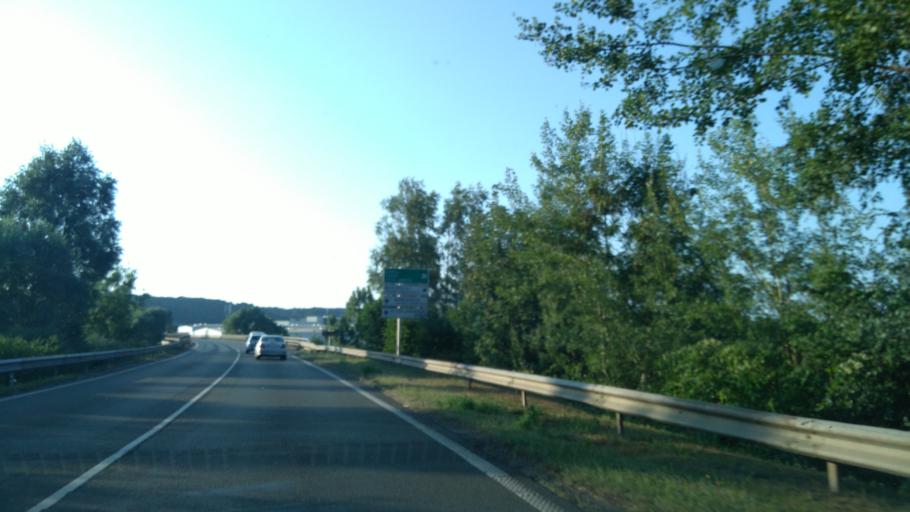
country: FR
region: Picardie
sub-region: Departement de l'Oise
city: Montataire
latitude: 49.2508
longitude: 2.4578
